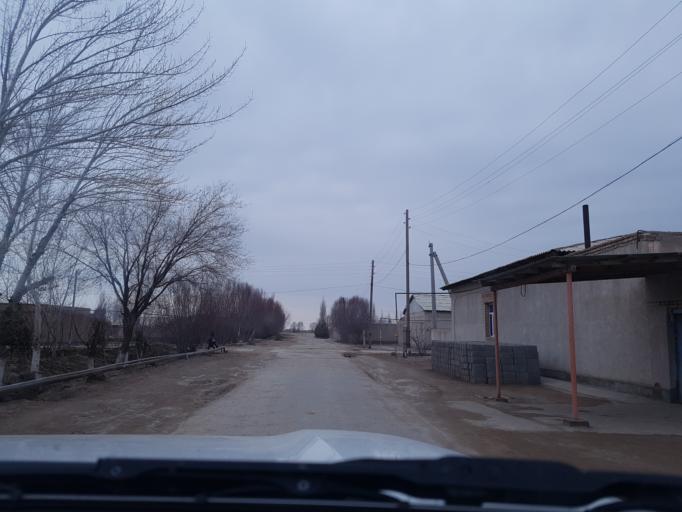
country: TM
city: Akdepe
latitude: 41.9829
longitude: 59.4694
